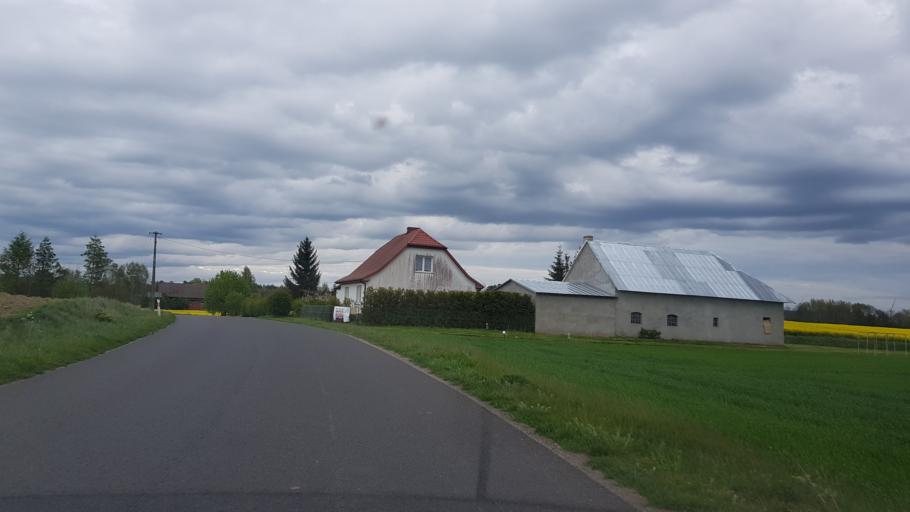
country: PL
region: West Pomeranian Voivodeship
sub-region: Powiat slawienski
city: Darlowo
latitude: 54.2729
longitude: 16.5068
